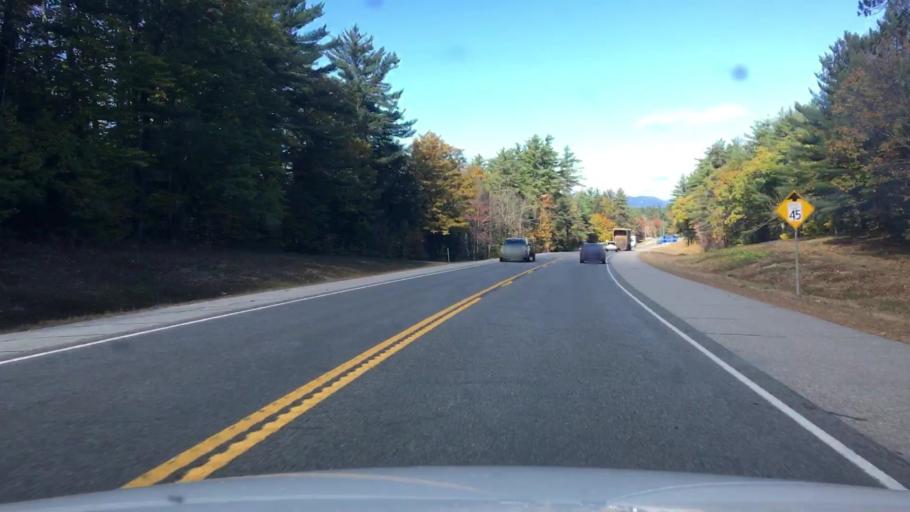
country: US
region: New Hampshire
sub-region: Carroll County
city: Ossipee
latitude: 43.7689
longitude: -71.1602
